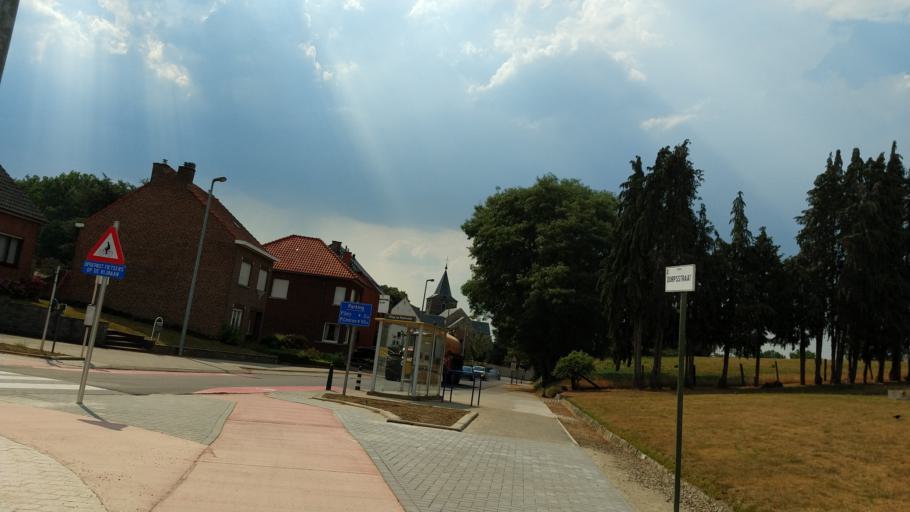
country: BE
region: Flanders
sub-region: Provincie Vlaams-Brabant
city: Bierbeek
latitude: 50.8272
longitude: 4.7631
